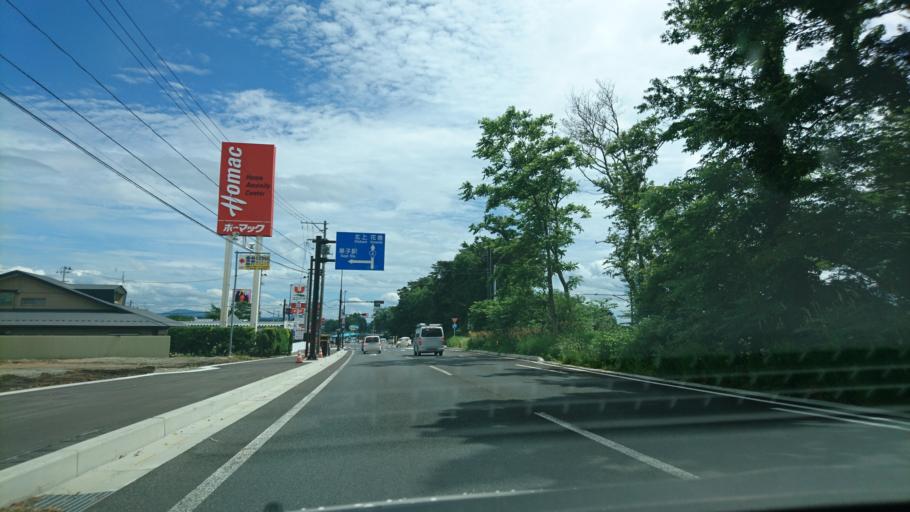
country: JP
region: Iwate
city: Morioka-shi
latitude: 39.7749
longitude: 141.1274
